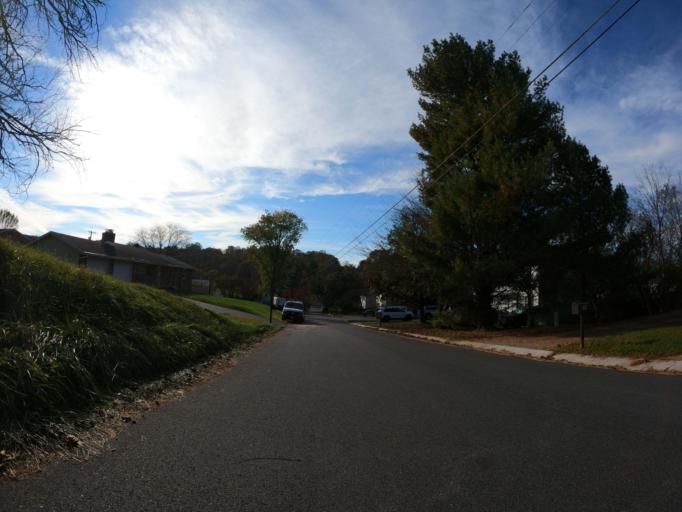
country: US
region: Maryland
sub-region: Carroll County
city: Sykesville
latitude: 39.3668
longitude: -76.9768
